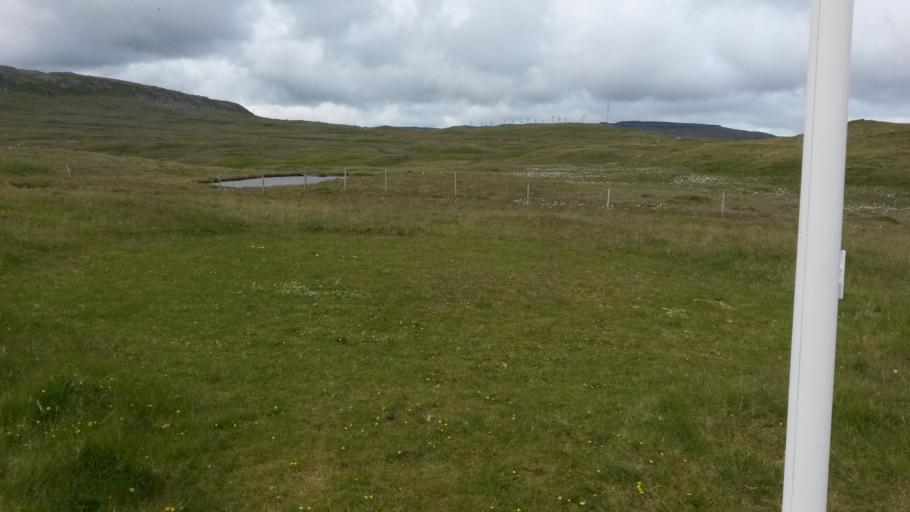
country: FO
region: Streymoy
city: Argir
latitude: 61.9912
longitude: -6.8522
